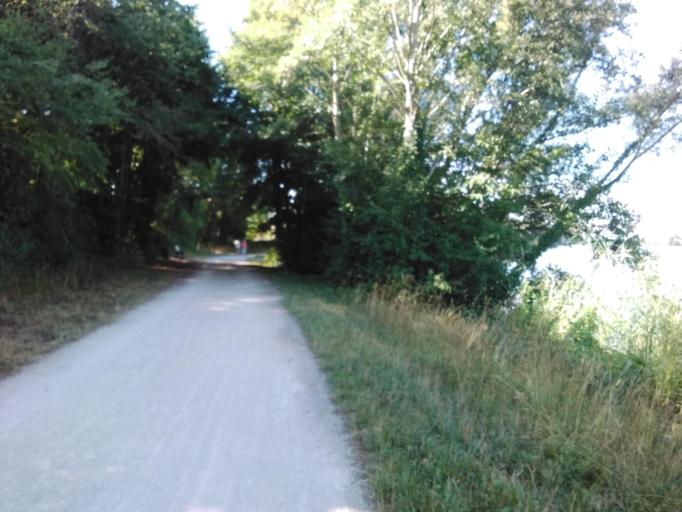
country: DE
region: Bavaria
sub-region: Regierungsbezirk Mittelfranken
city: Allersberg
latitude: 49.2390
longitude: 11.2087
